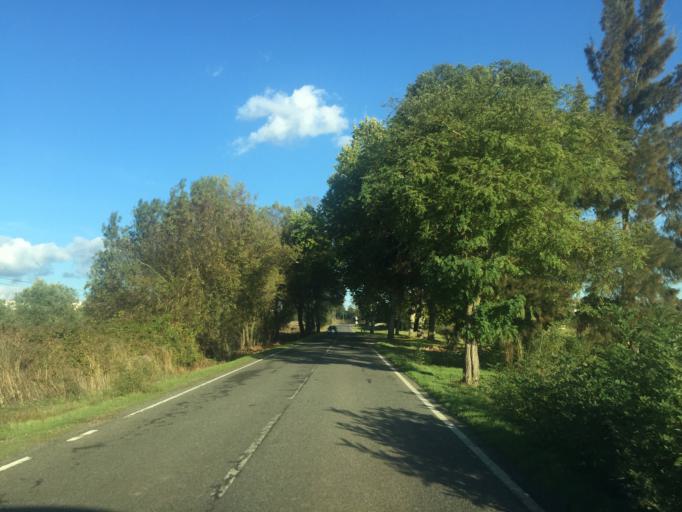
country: PT
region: Portalegre
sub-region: Alter do Chao
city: Alter do Chao
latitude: 39.1962
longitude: -7.6748
